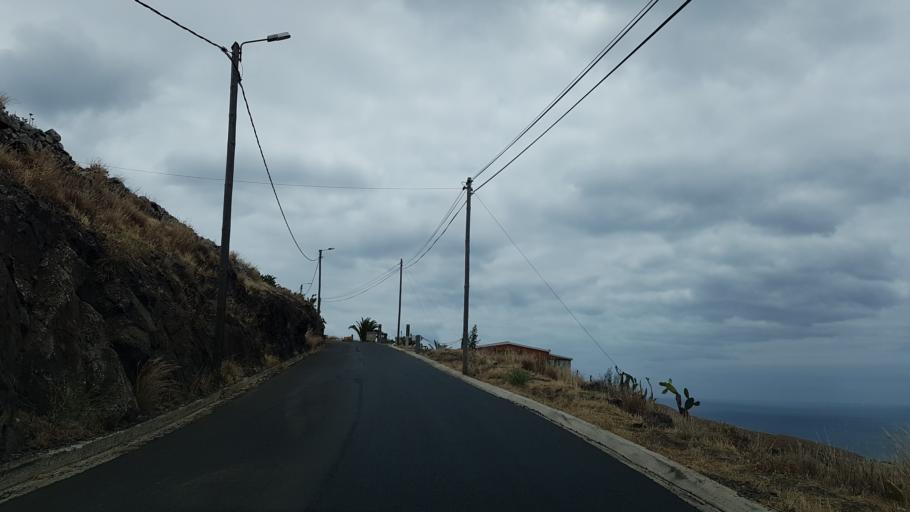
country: PT
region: Madeira
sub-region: Porto Santo
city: Vila de Porto Santo
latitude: 33.0695
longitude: -16.3215
